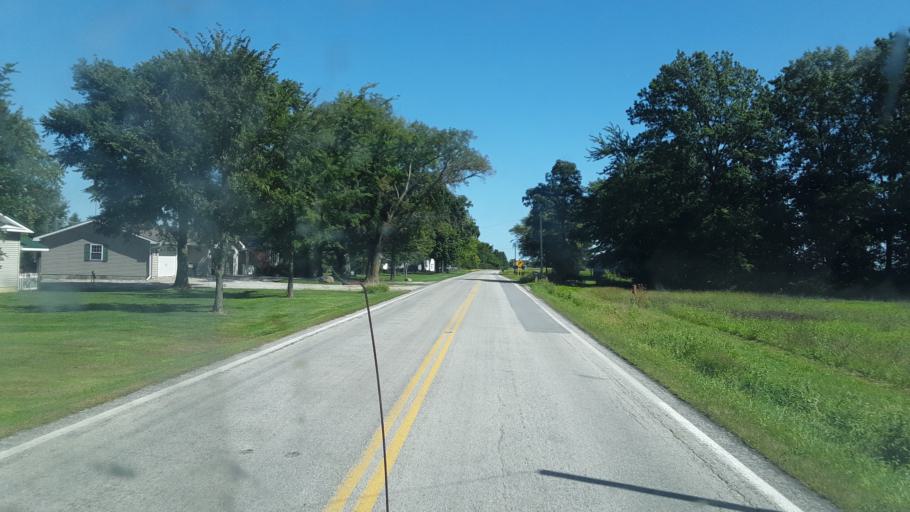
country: US
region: Ohio
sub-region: Huron County
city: Monroeville
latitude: 41.2363
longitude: -82.7347
